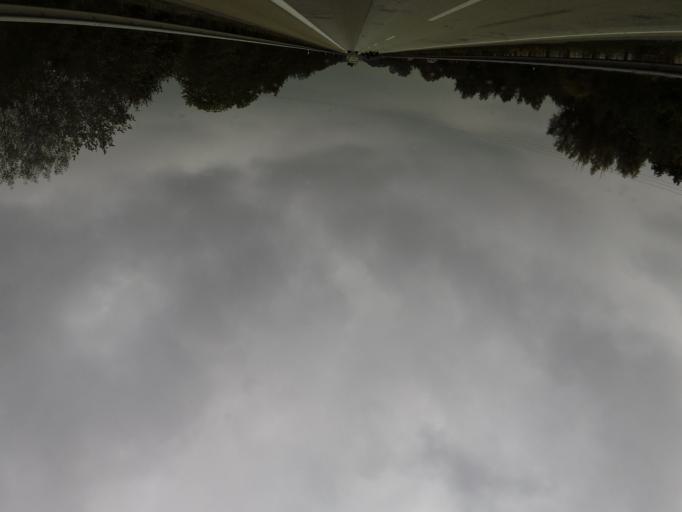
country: DE
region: Rheinland-Pfalz
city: Hauptstuhl
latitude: 49.4054
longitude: 7.4873
